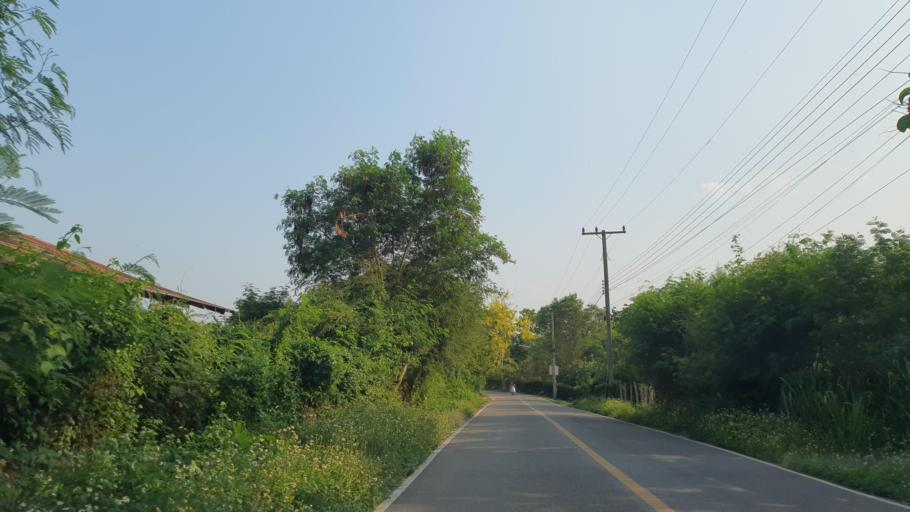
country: TH
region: Chiang Mai
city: Mae Wang
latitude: 18.6502
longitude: 98.8138
